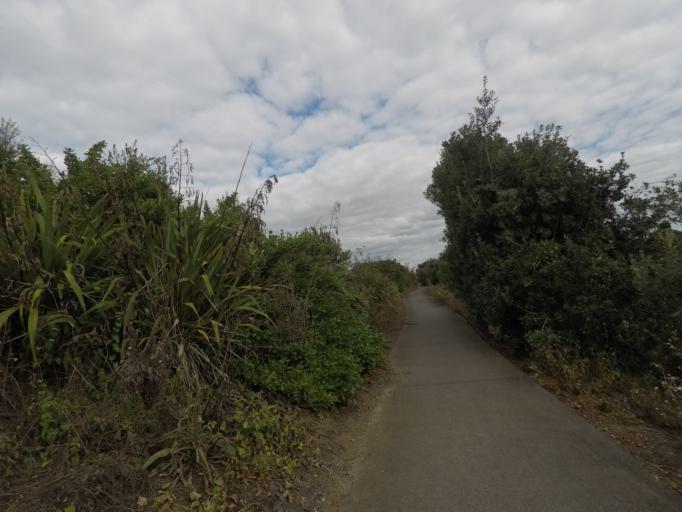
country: NZ
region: Auckland
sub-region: Auckland
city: Papakura
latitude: -37.0531
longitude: 174.9266
